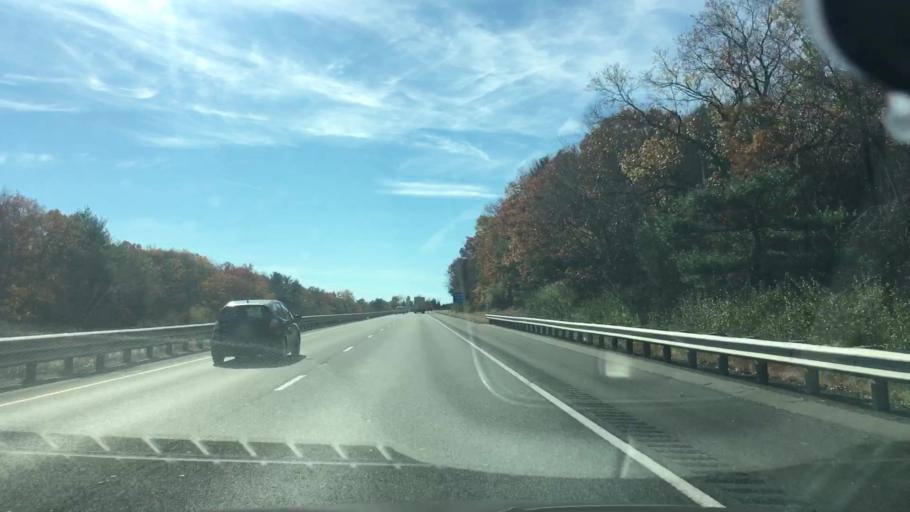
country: US
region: Massachusetts
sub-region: Hampshire County
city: South Hadley
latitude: 42.2623
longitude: -72.6149
